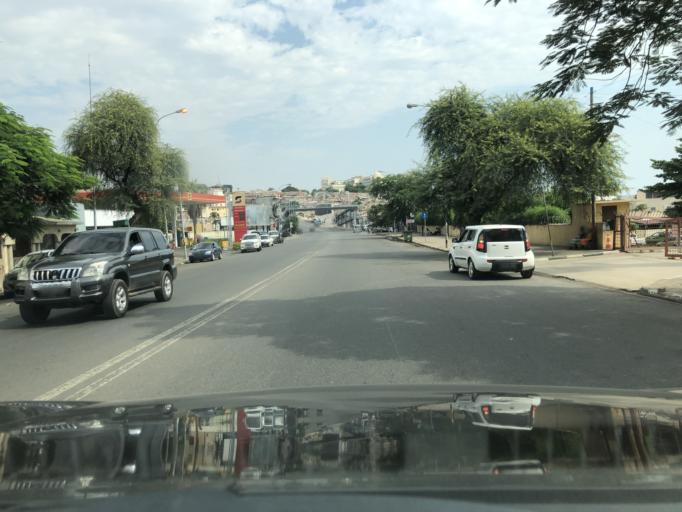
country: AO
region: Luanda
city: Luanda
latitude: -8.8279
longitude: 13.2266
